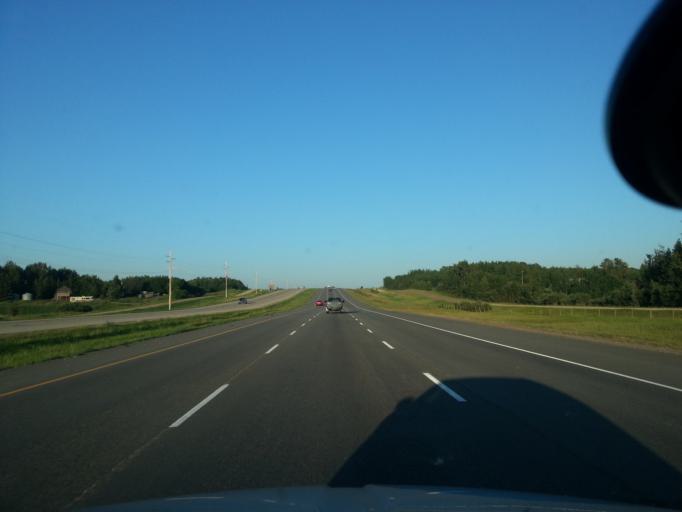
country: CA
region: Alberta
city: Stony Plain
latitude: 53.5701
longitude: -114.1960
